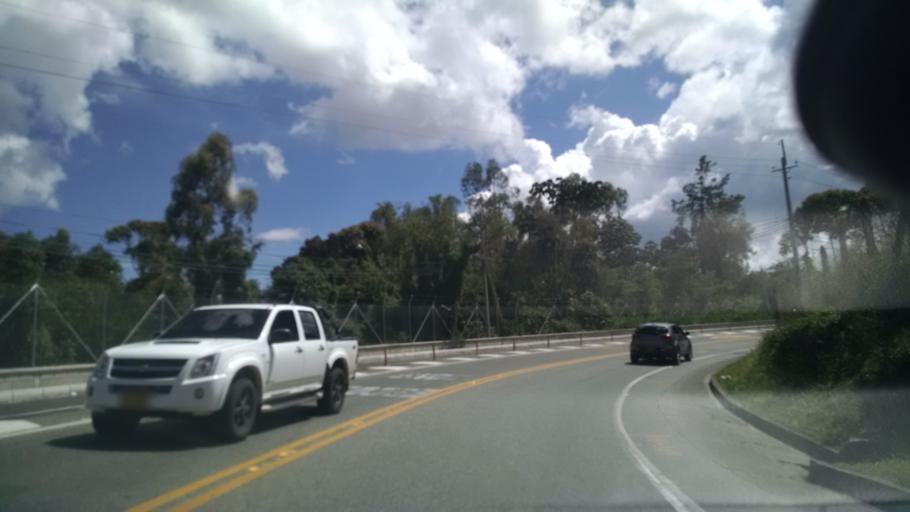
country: CO
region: Antioquia
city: El Retiro
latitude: 6.1080
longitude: -75.5009
